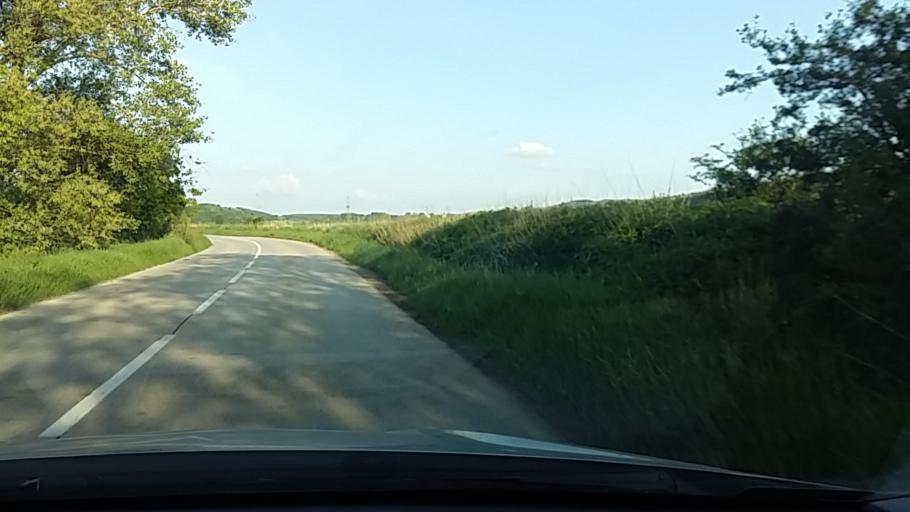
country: HU
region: Pest
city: Szod
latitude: 47.7566
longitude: 19.1895
